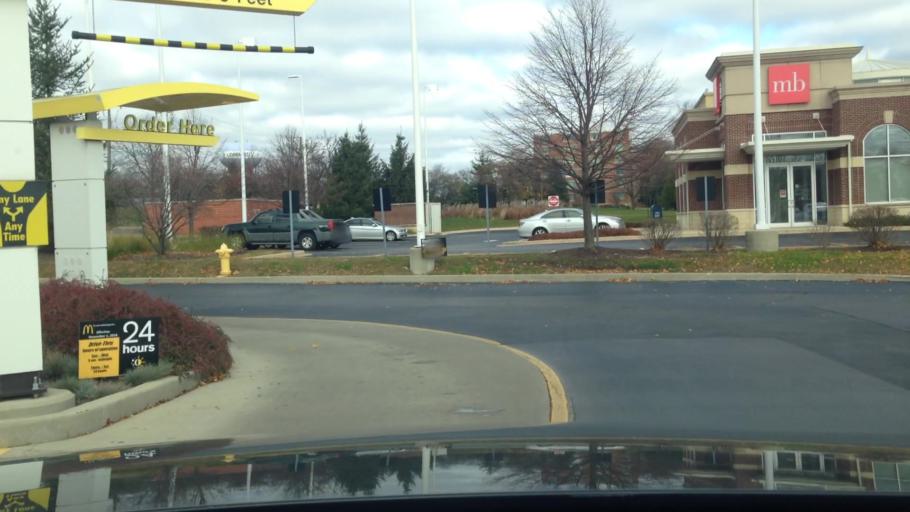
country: US
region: Illinois
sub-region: DuPage County
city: Downers Grove
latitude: 41.8422
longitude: -88.0107
